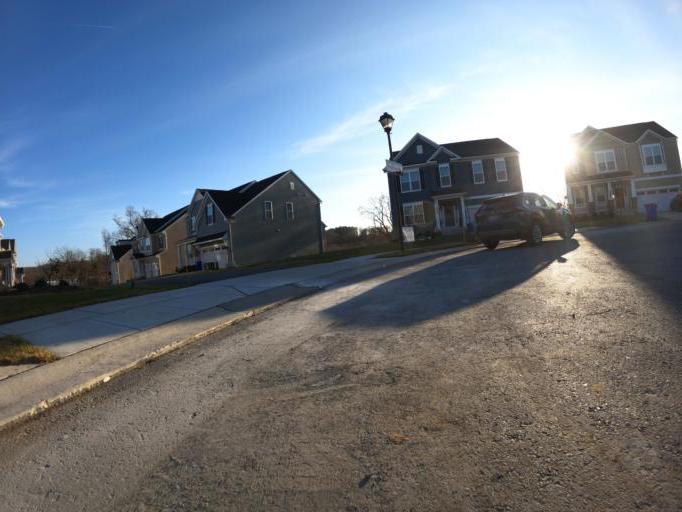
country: US
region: Maryland
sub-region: Howard County
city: Highland
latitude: 39.1959
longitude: -76.9398
